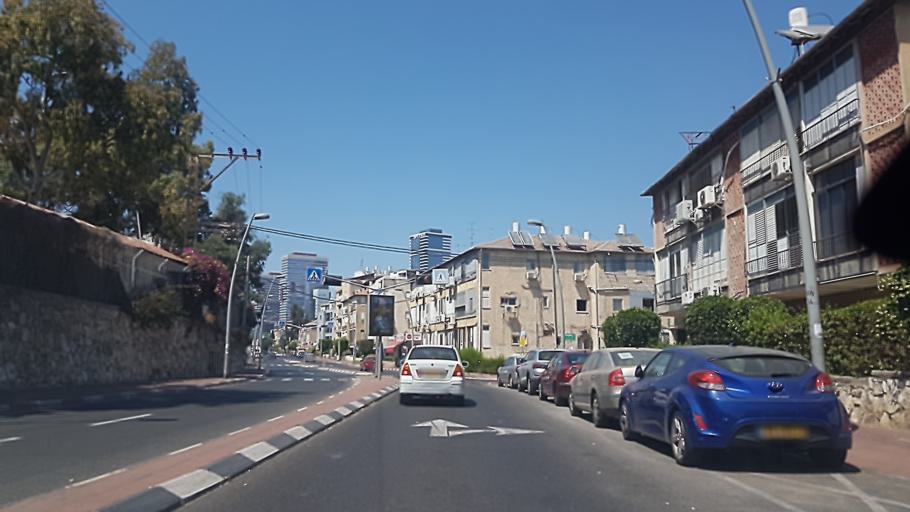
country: IL
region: Tel Aviv
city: Ramat Gan
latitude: 32.0845
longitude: 34.8220
